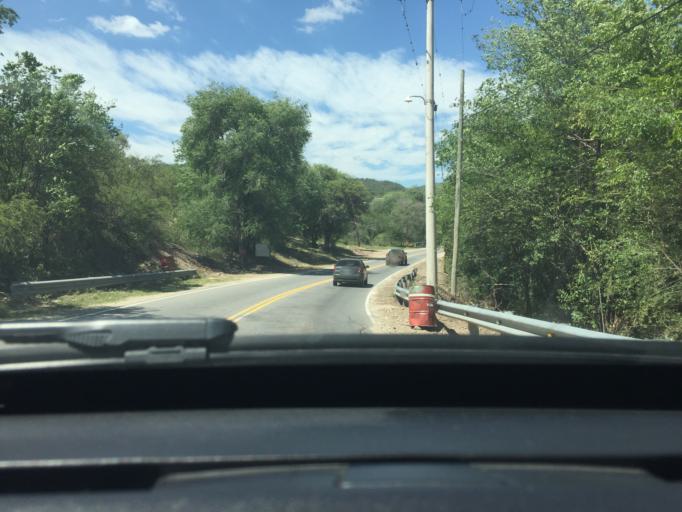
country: AR
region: Cordoba
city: Alta Gracia
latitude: -31.7348
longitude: -64.4498
